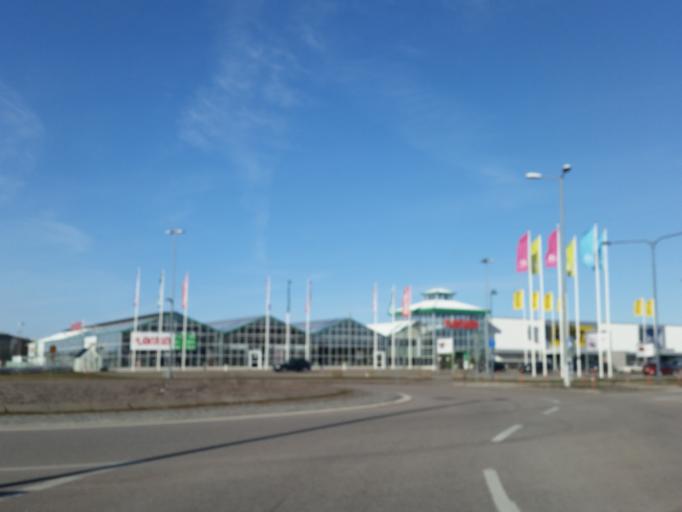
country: SE
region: Kalmar
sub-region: Kalmar Kommun
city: Lindsdal
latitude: 56.6860
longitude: 16.3144
